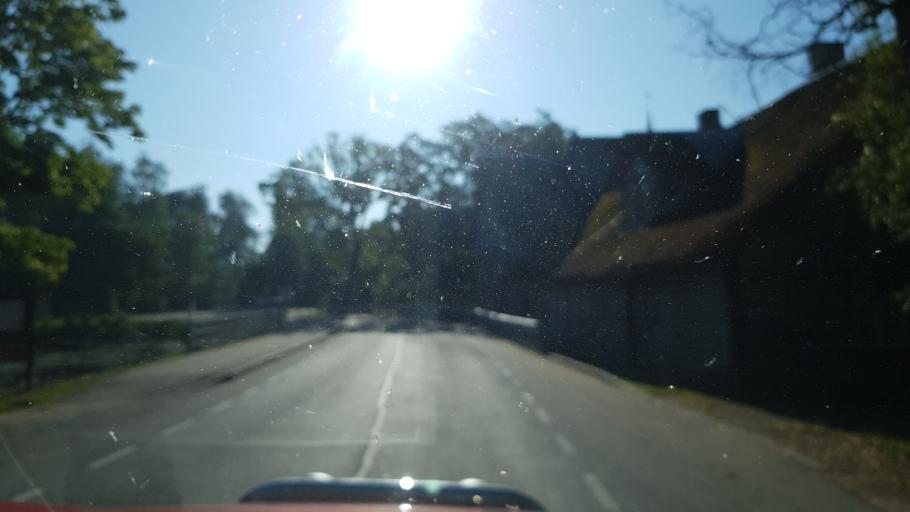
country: EE
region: Jogevamaa
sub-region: Tabivere vald
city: Tabivere
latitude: 58.6847
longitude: 26.5812
